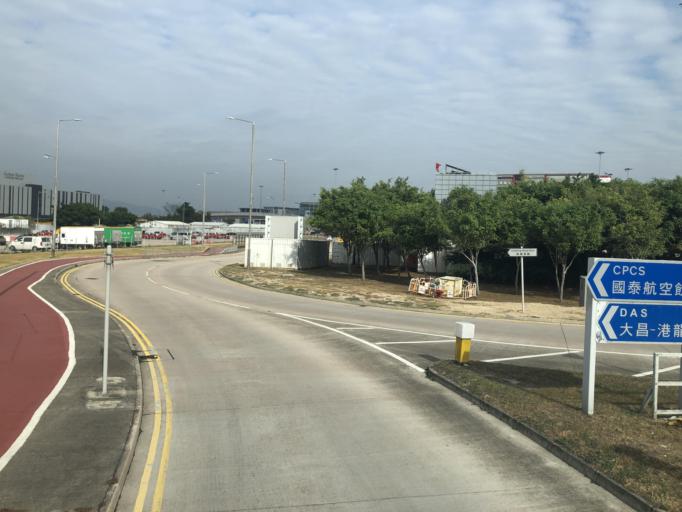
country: HK
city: Tai O
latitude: 22.2996
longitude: 113.9324
